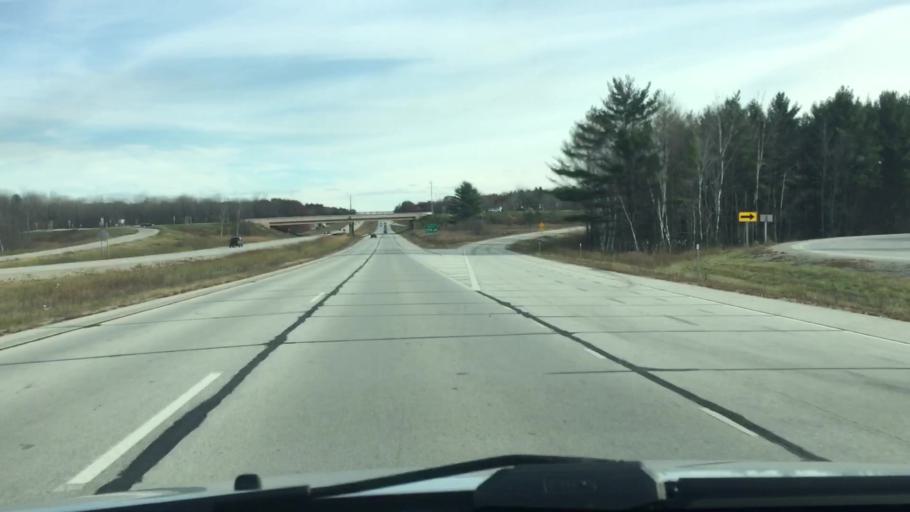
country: US
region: Wisconsin
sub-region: Brown County
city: Howard
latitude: 44.5621
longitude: -88.1347
